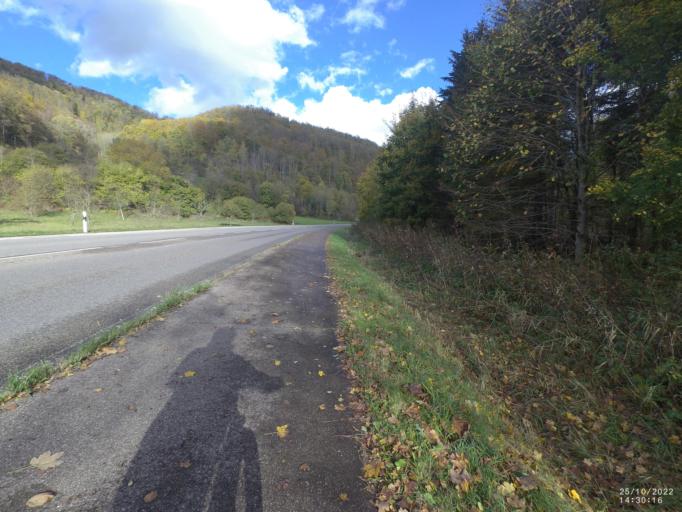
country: DE
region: Baden-Wuerttemberg
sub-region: Regierungsbezirk Stuttgart
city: Geislingen an der Steige
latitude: 48.6426
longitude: 9.8783
